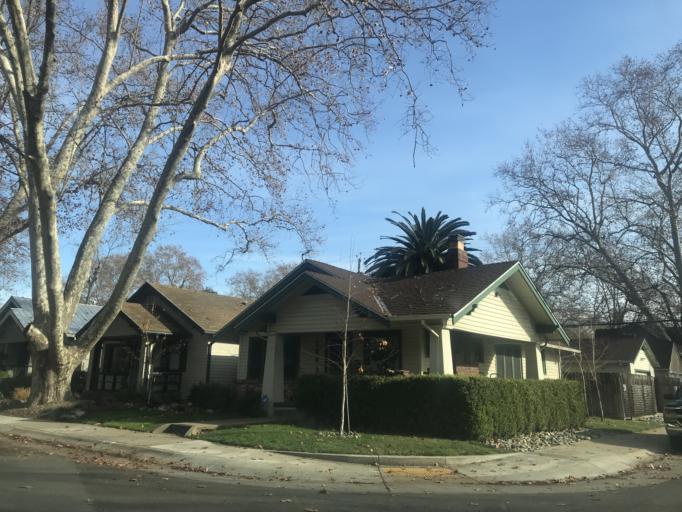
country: US
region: California
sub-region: Sacramento County
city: Sacramento
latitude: 38.5588
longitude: -121.4924
